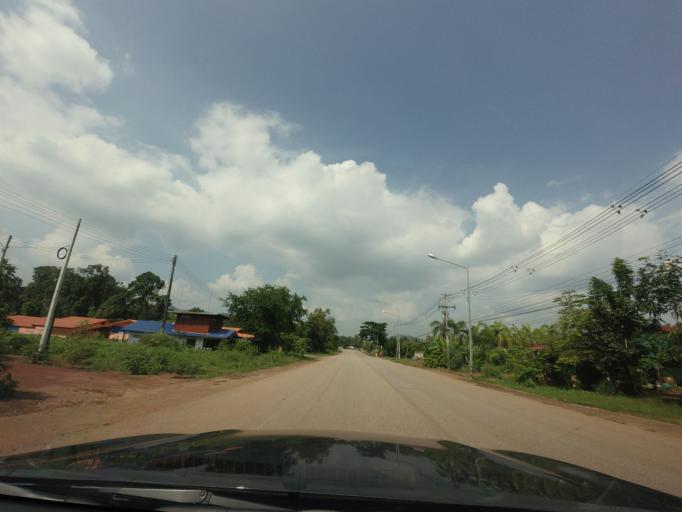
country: TH
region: Uttaradit
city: Ban Khok
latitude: 18.0248
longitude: 101.0732
